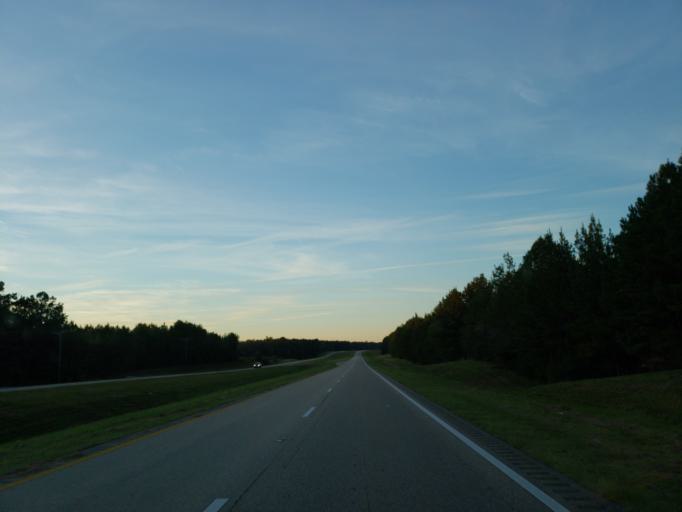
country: US
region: Mississippi
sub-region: Wayne County
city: Belmont
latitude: 31.4824
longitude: -88.4847
